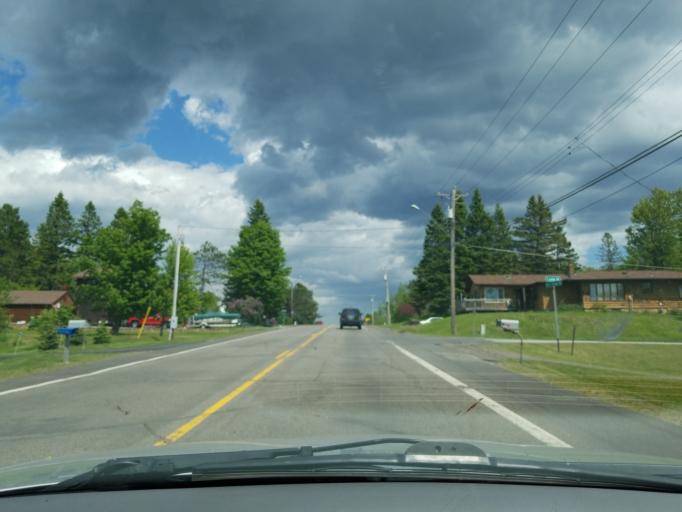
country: US
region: Minnesota
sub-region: Saint Louis County
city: Proctor
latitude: 46.7785
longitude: -92.1786
